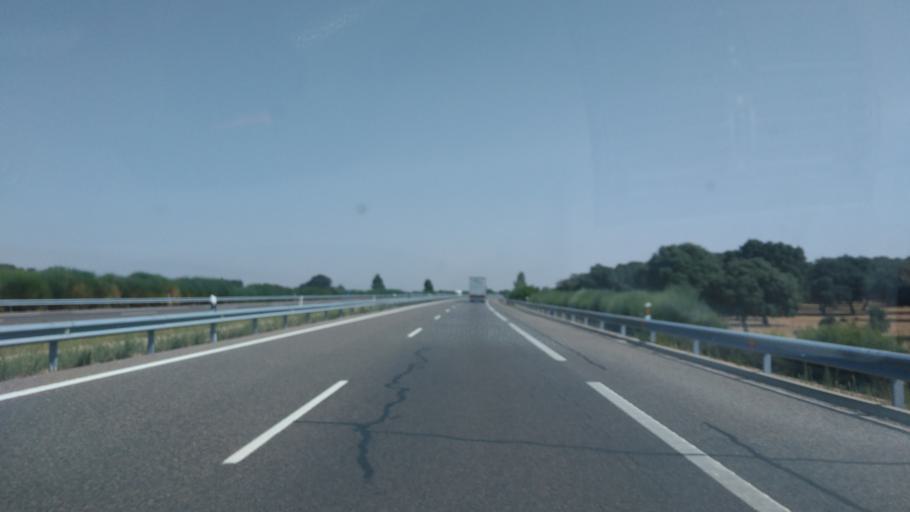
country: ES
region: Castille and Leon
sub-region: Provincia de Salamanca
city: La Fuente de San Esteban
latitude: 40.7992
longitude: -6.2068
